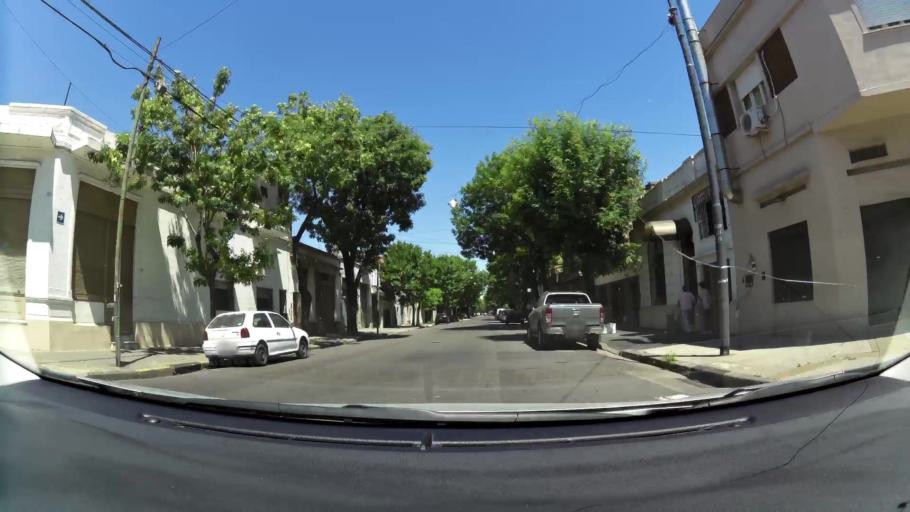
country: AR
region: Buenos Aires
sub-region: Partido de Avellaneda
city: Avellaneda
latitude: -34.6464
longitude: -58.4110
